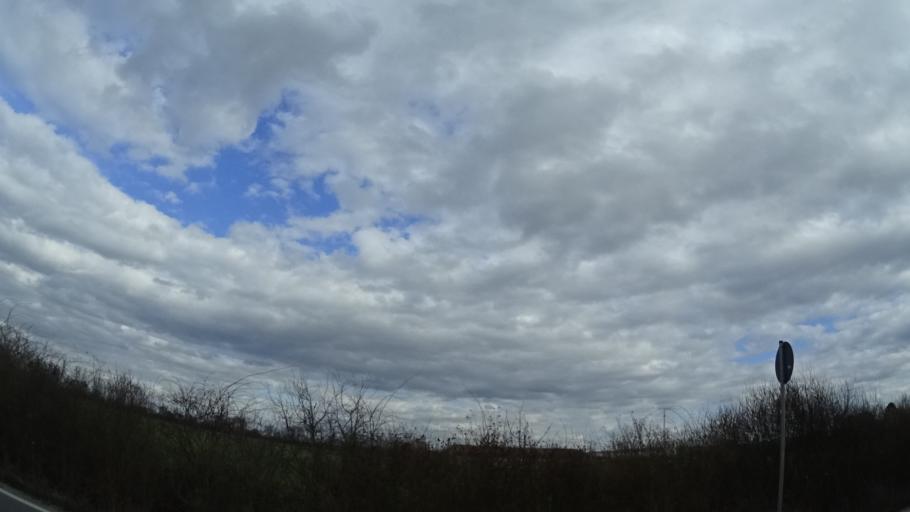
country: DE
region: Hesse
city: Biebesheim
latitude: 49.7837
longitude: 8.4898
